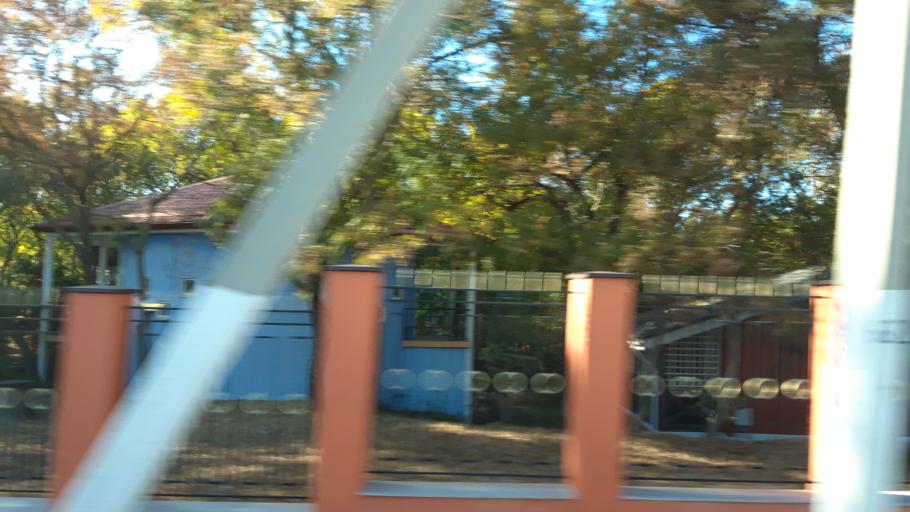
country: RU
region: Krasnodarskiy
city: Kabardinka
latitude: 44.6461
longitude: 37.9381
